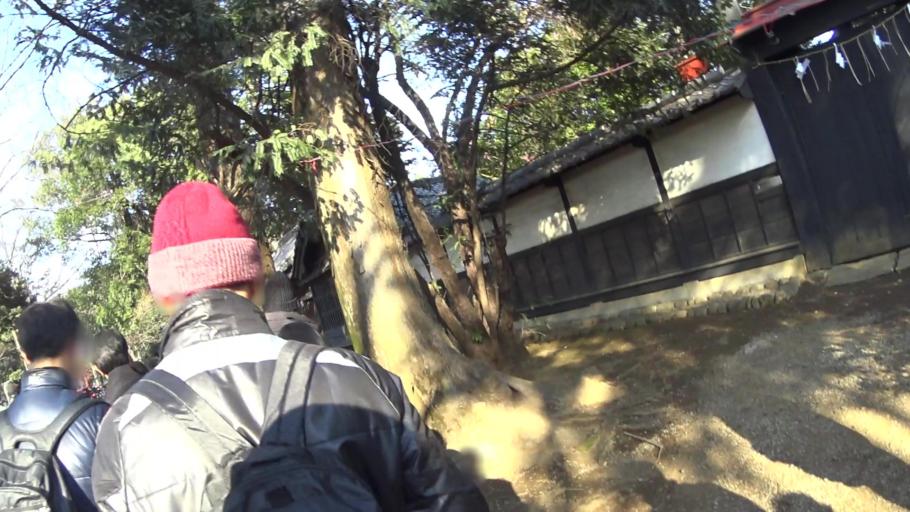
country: JP
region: Saitama
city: Saitama
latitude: 35.9141
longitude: 139.6311
